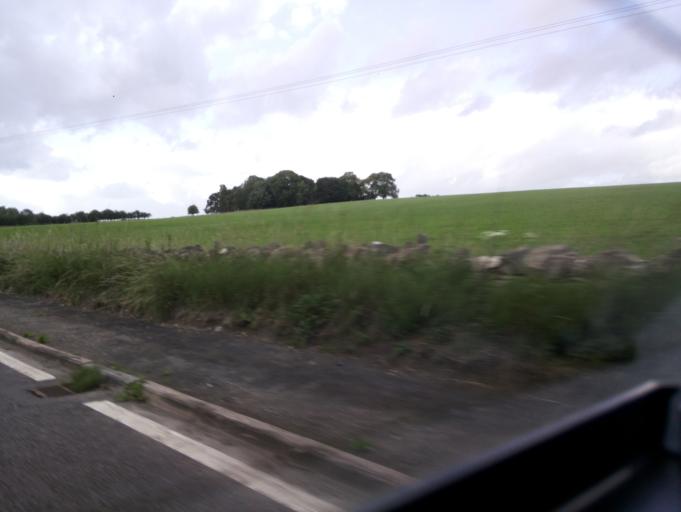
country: GB
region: England
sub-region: Gloucestershire
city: Shipton Village
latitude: 51.8699
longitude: -1.9633
